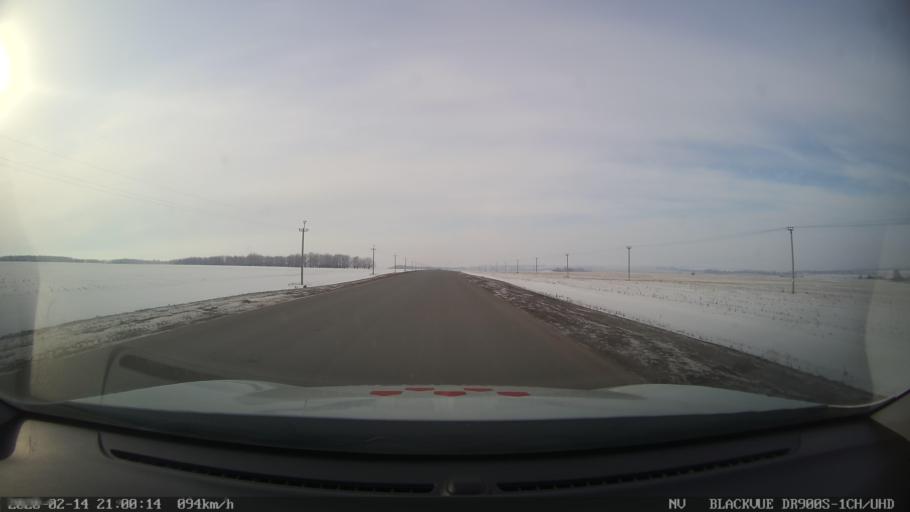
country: RU
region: Tatarstan
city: Kuybyshevskiy Zaton
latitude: 55.1726
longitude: 49.2239
